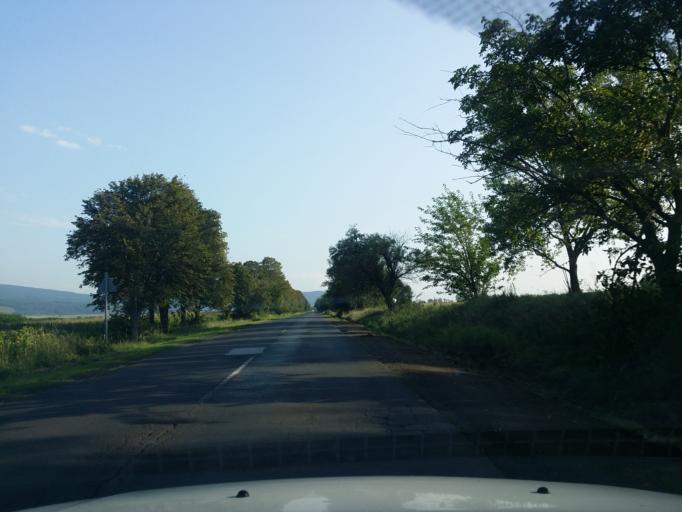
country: HU
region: Borsod-Abauj-Zemplen
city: Abaujszanto
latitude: 48.3196
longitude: 21.2006
